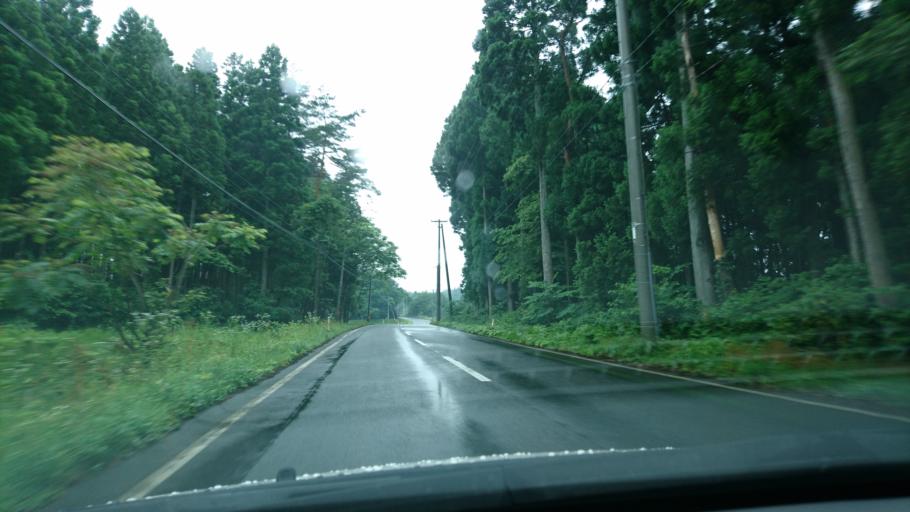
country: JP
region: Iwate
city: Ichinoseki
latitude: 38.9370
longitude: 141.0364
